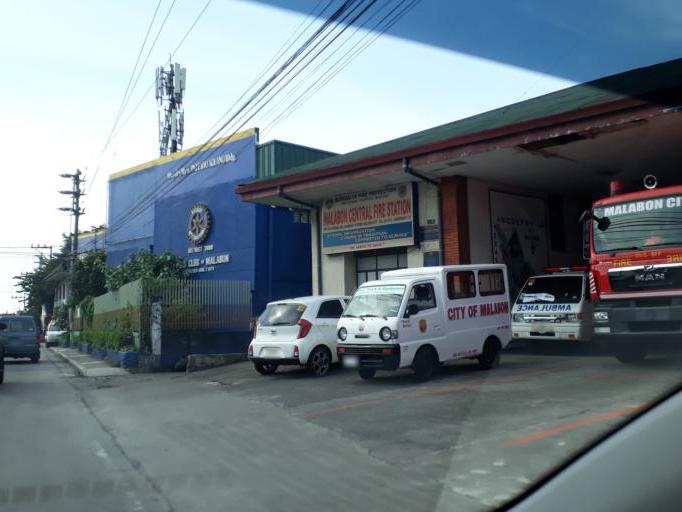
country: PH
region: Metro Manila
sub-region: Caloocan City
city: Niugan
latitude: 14.6689
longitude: 120.9760
